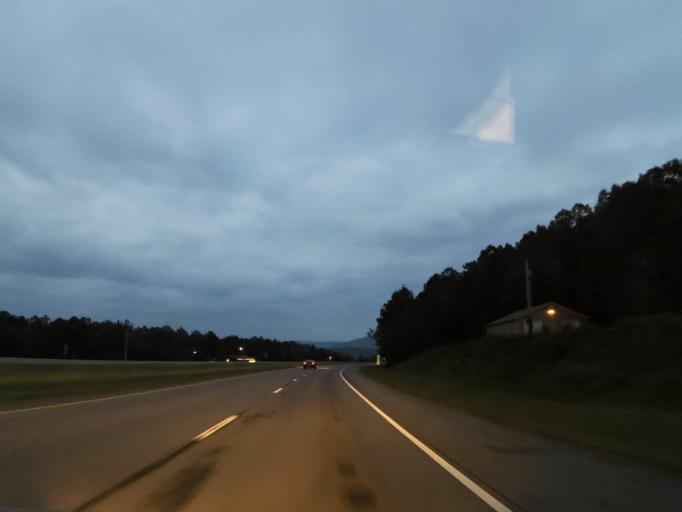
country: US
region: Alabama
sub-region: Madison County
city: Owens Cross Roads
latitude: 34.6943
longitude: -86.3631
